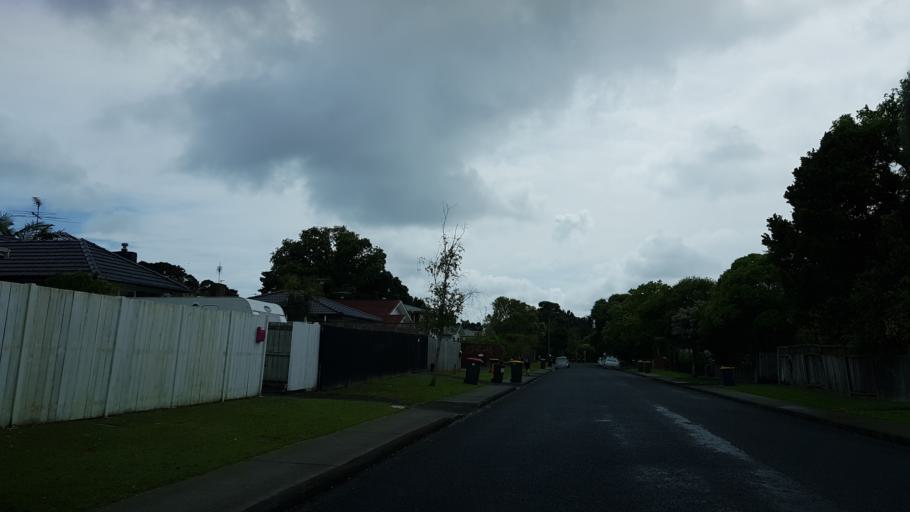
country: NZ
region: Auckland
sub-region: Auckland
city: North Shore
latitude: -36.7942
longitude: 174.7385
